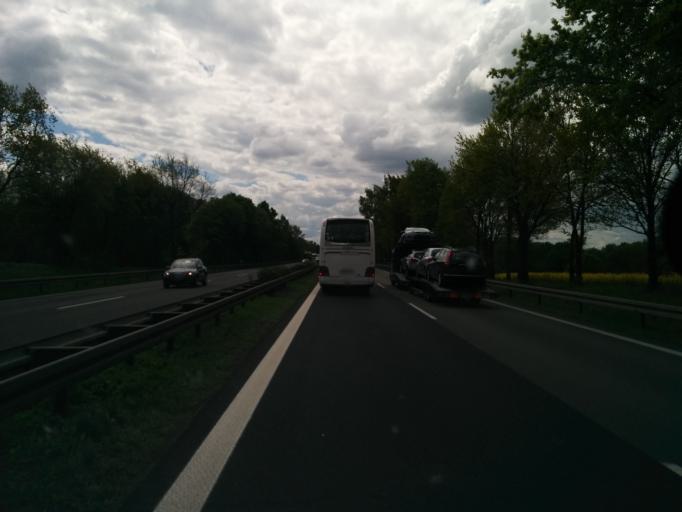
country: DE
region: Brandenburg
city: Werder
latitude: 52.4588
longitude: 12.9382
